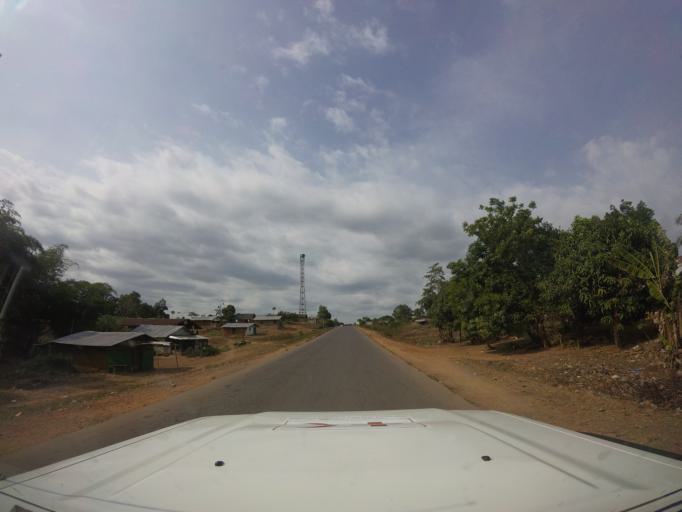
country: LR
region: Bomi
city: Tubmanburg
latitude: 6.6926
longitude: -10.8743
